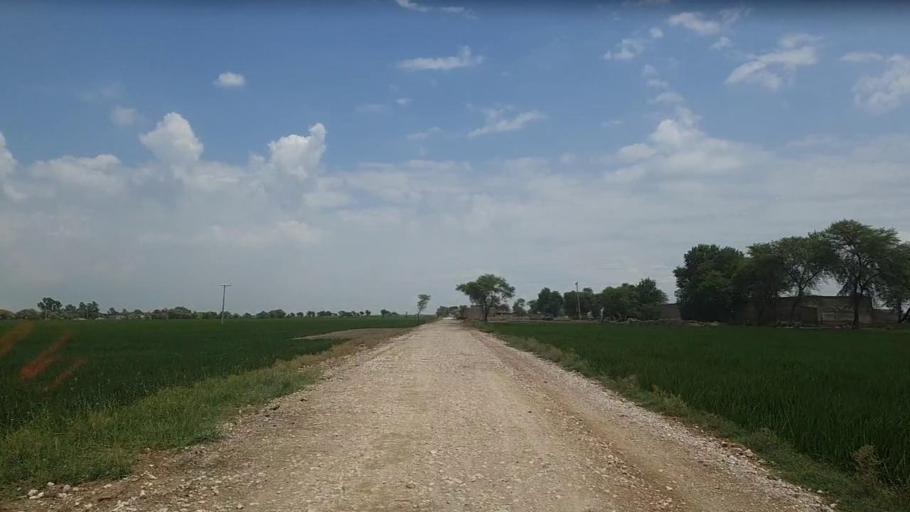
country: PK
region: Sindh
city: Kandhkot
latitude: 28.3422
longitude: 69.2132
